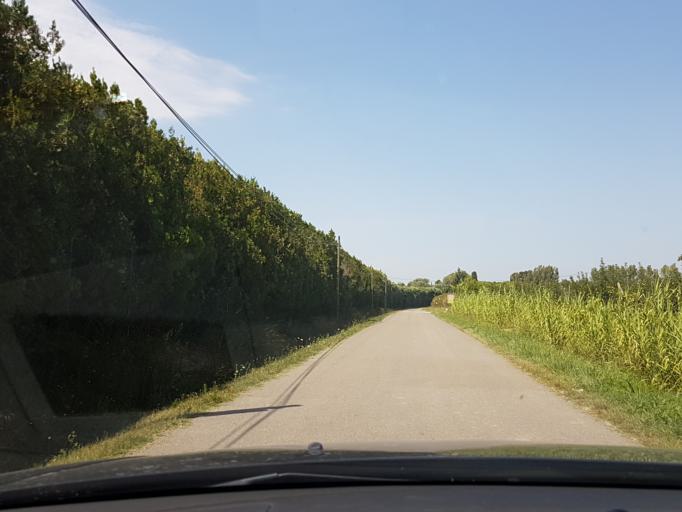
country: FR
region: Provence-Alpes-Cote d'Azur
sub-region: Departement des Bouches-du-Rhone
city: Saint-Remy-de-Provence
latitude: 43.7915
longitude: 4.8706
